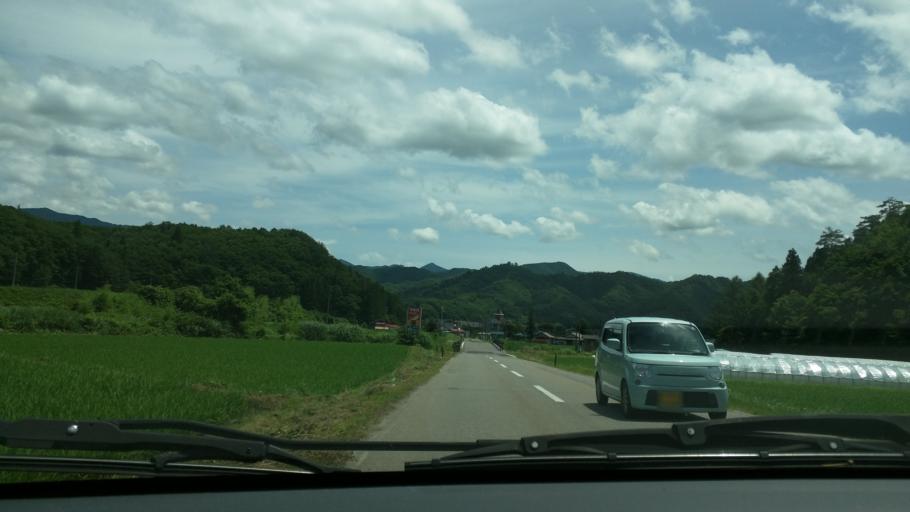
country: JP
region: Tochigi
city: Kuroiso
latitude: 37.2126
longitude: 139.7553
